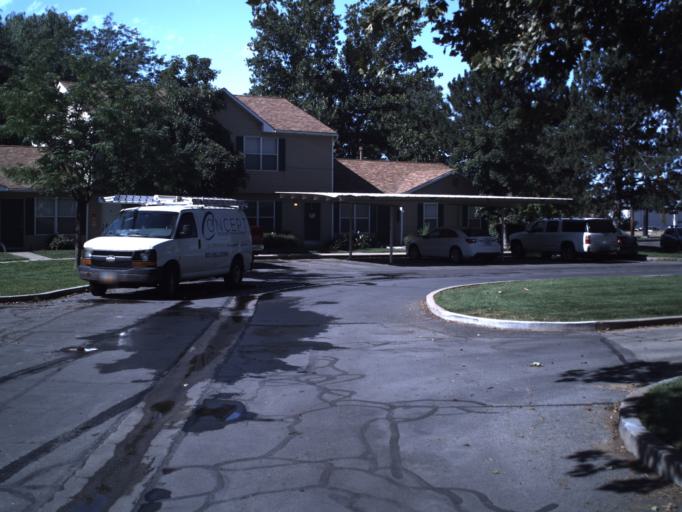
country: US
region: Utah
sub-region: Davis County
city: Layton
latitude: 41.0563
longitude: -111.9566
